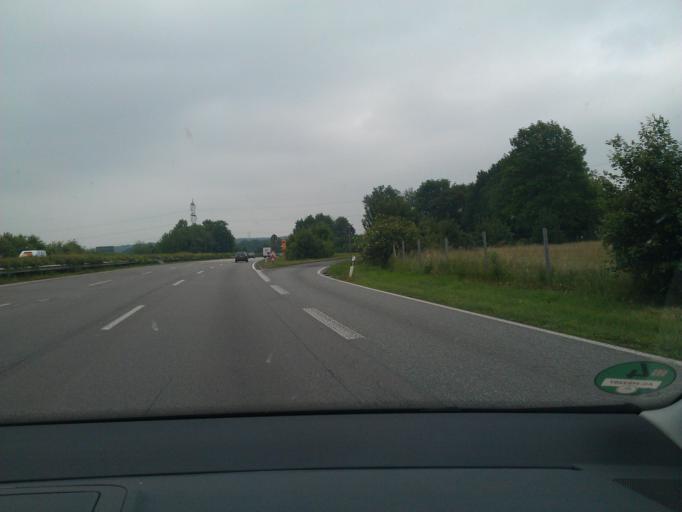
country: DE
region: Rheinland-Pfalz
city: Weitersburg
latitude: 50.4150
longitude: 7.6098
